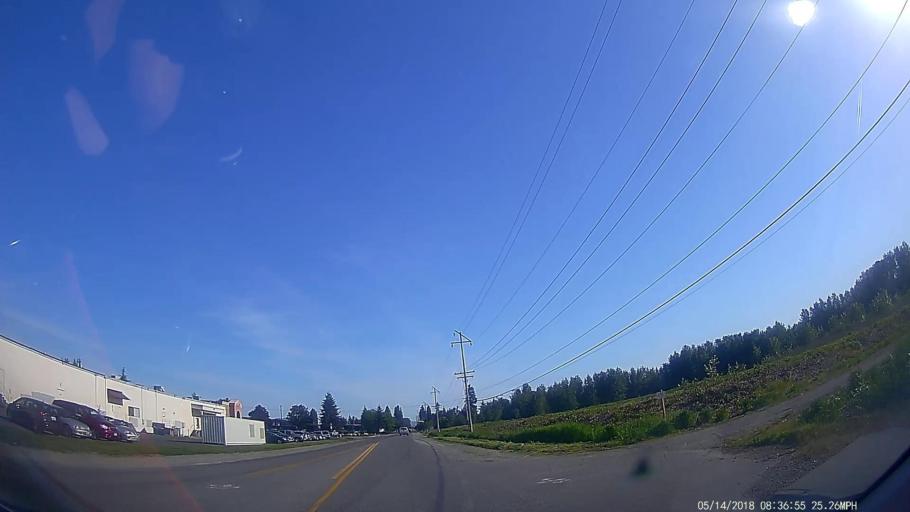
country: US
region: Washington
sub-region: Skagit County
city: Mount Vernon
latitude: 48.4373
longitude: -122.3322
